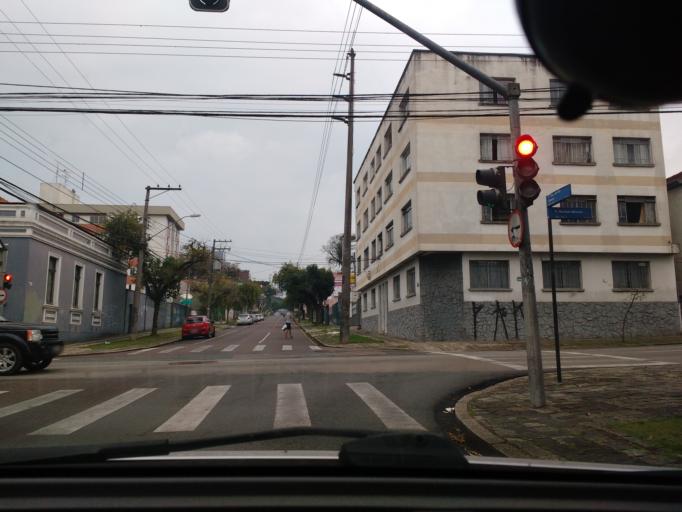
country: BR
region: Parana
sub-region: Curitiba
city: Curitiba
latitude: -25.4276
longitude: -49.2823
